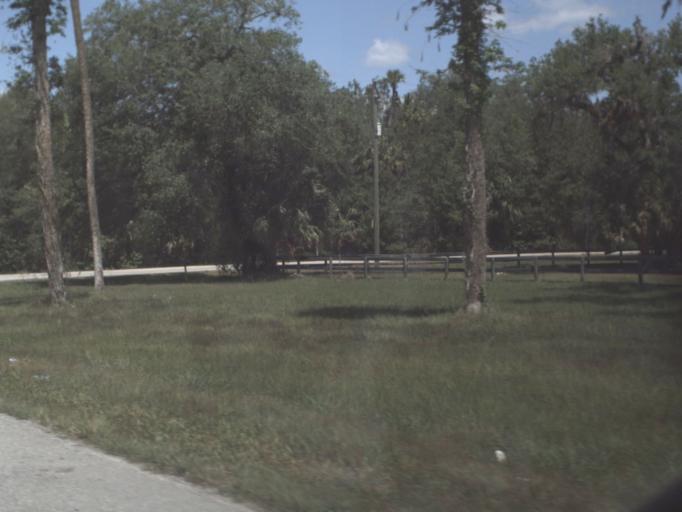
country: US
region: Florida
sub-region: Marion County
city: Silver Springs Shores
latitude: 29.2180
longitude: -82.0152
